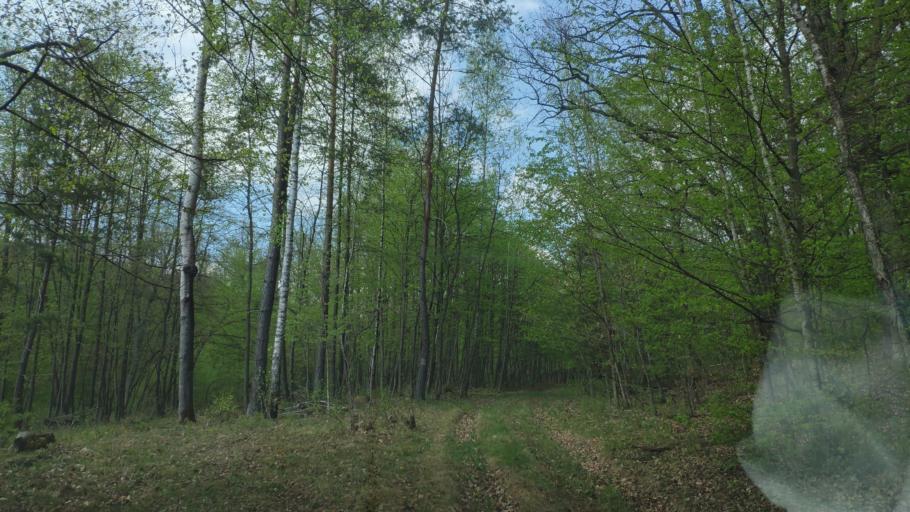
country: SK
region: Kosicky
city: Moldava nad Bodvou
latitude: 48.5377
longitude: 20.9422
